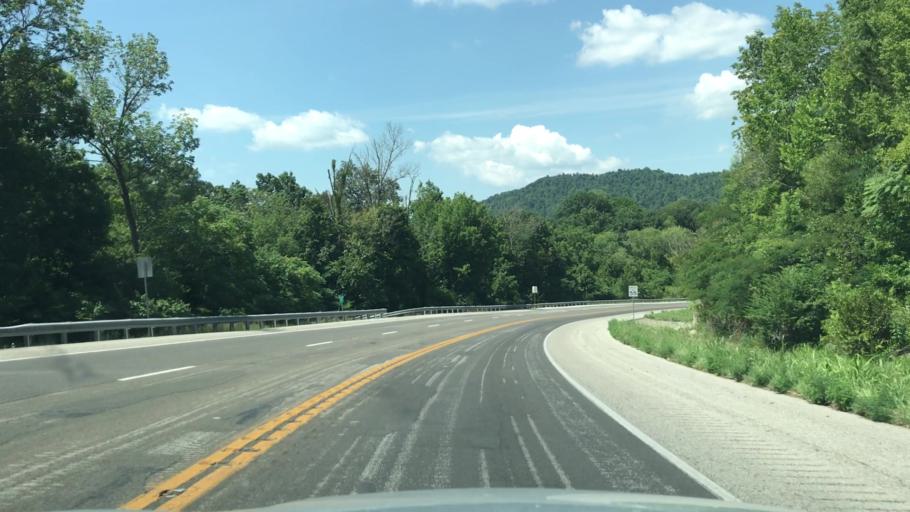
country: US
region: Kentucky
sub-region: Wayne County
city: Monticello
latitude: 36.8169
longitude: -84.8747
